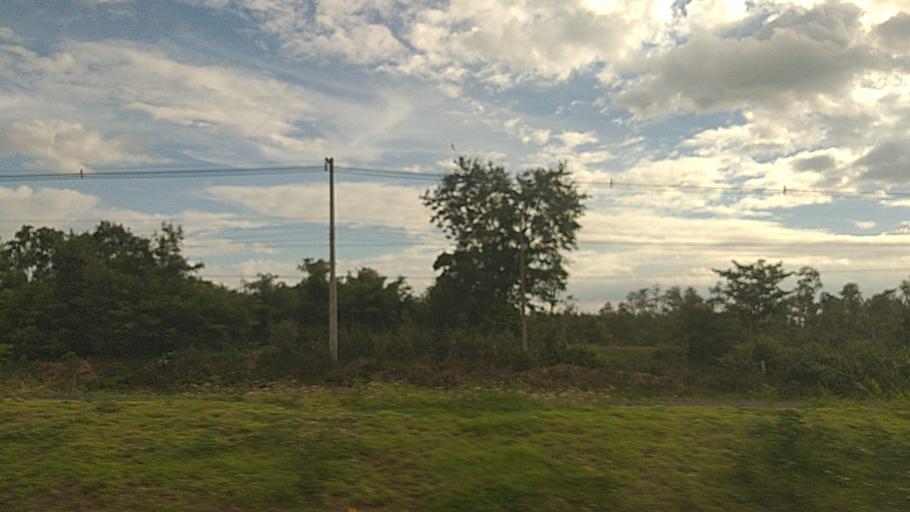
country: TH
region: Surin
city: Kap Choeng
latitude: 14.5217
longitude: 103.5406
